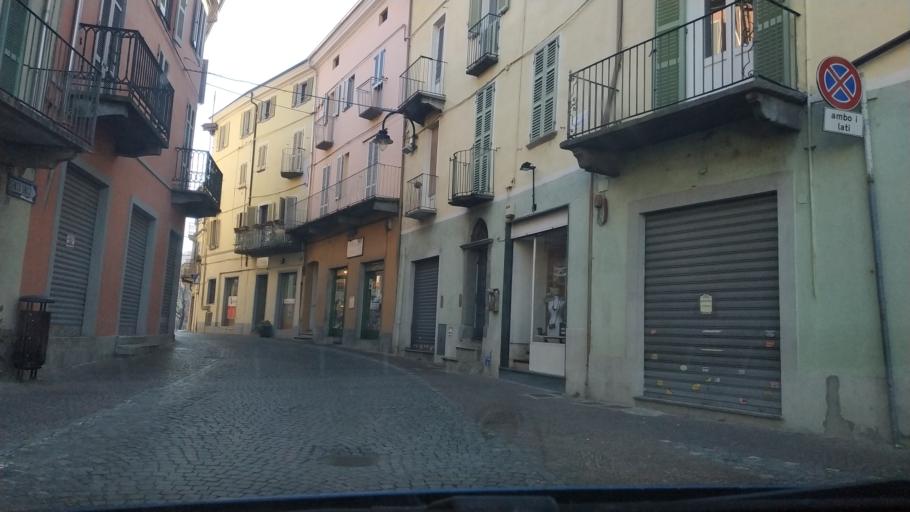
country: IT
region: Piedmont
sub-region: Provincia di Torino
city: Ivrea
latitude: 45.4642
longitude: 7.8711
